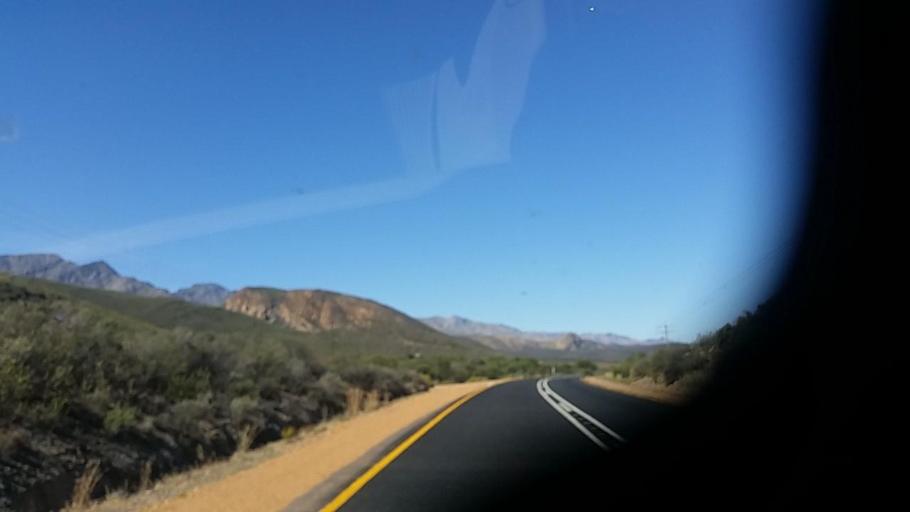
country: ZA
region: Western Cape
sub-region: Eden District Municipality
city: Oudtshoorn
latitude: -33.4780
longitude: 22.6328
